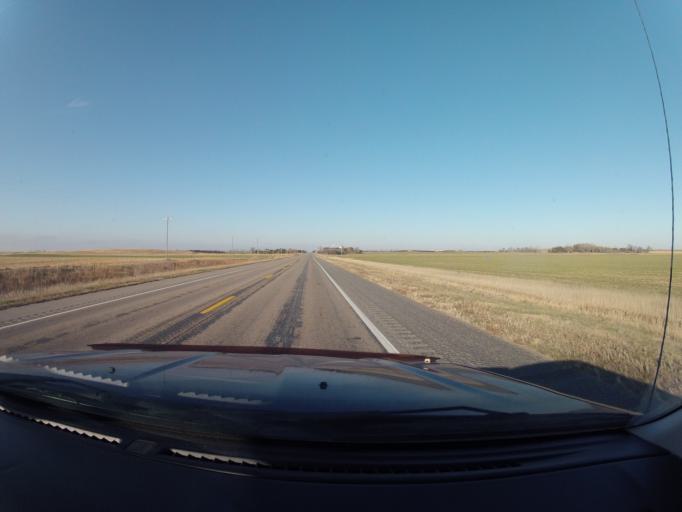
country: US
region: Nebraska
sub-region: Kearney County
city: Minden
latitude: 40.5884
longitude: -98.9516
